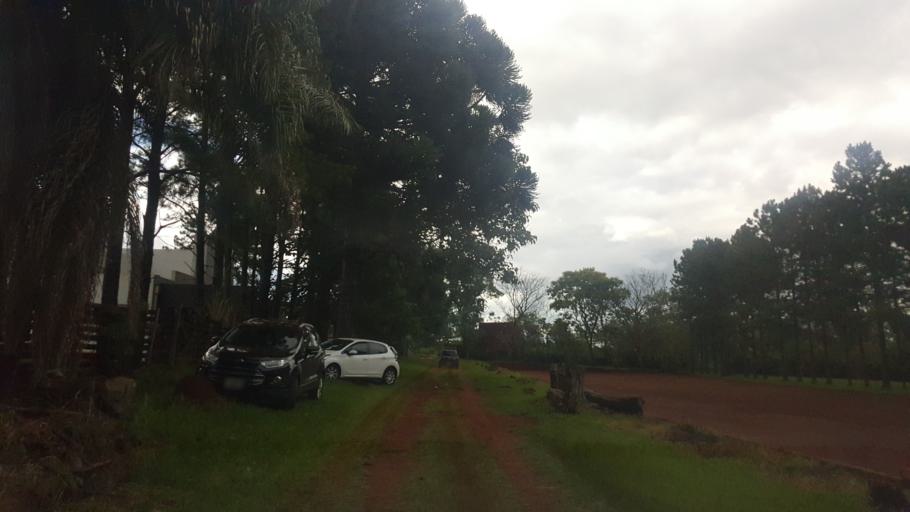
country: AR
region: Misiones
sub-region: Departamento de Capital
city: Posadas
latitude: -27.4051
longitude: -55.9692
